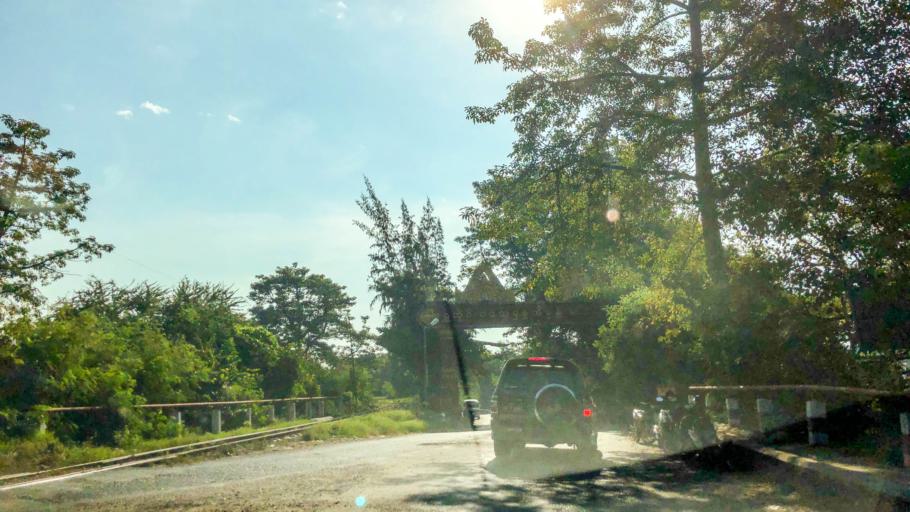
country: MM
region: Sagain
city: Sagaing
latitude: 21.8680
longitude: 95.9961
